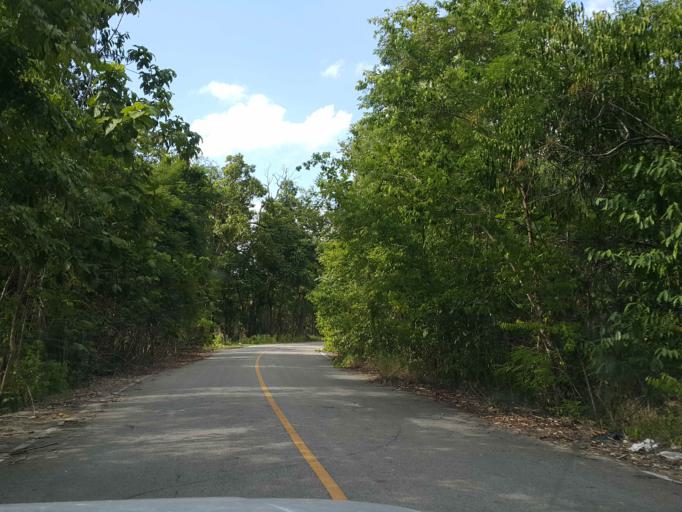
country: TH
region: Lampang
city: Thoen
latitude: 17.6418
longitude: 99.2845
